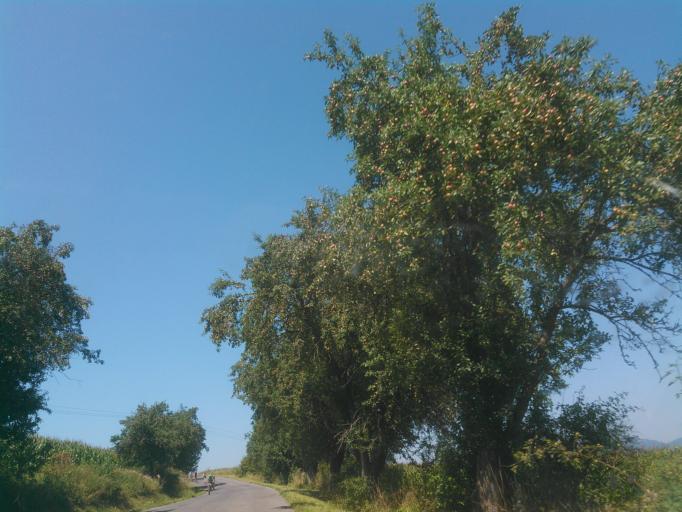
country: SK
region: Zilinsky
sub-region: Okres Liptovsky Mikulas
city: Liptovsky Mikulas
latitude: 49.0455
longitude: 19.4906
